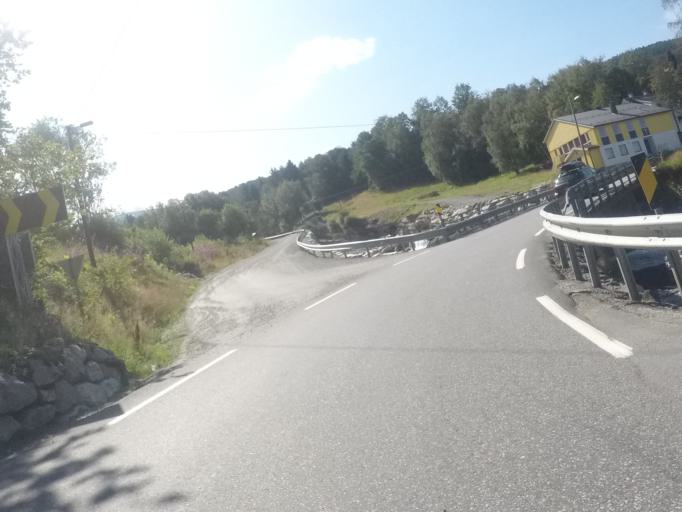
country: NO
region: Sogn og Fjordane
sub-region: Hornindal
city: Hornindal
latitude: 61.8039
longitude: 6.5276
